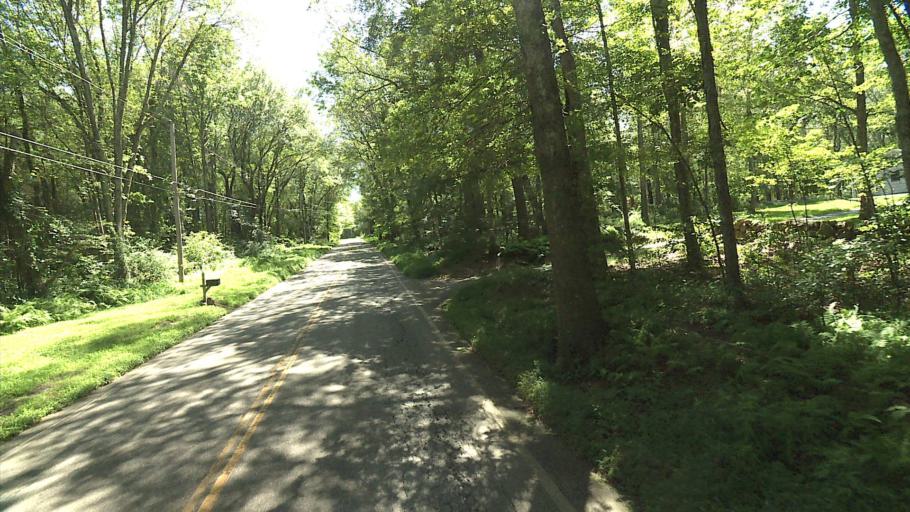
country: US
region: Connecticut
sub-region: Windham County
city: Windham
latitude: 41.7304
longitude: -72.0676
